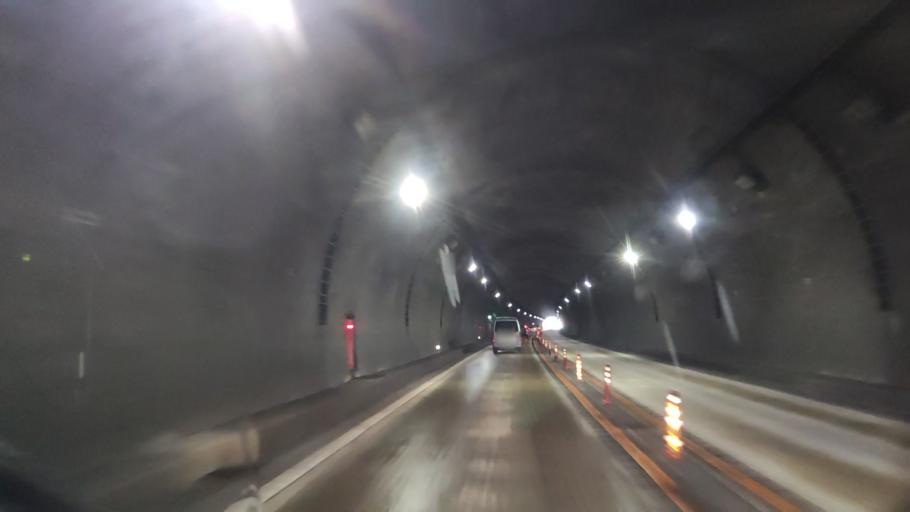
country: JP
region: Tokushima
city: Kamojimacho-jogejima
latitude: 34.1059
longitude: 134.2933
